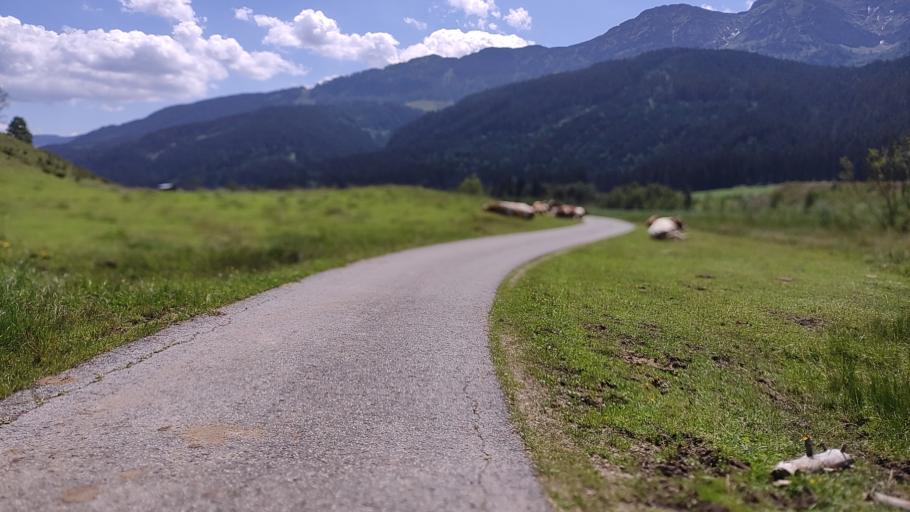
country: AT
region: Tyrol
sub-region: Politischer Bezirk Kitzbuhel
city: Hochfilzen
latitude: 47.4634
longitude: 12.6416
